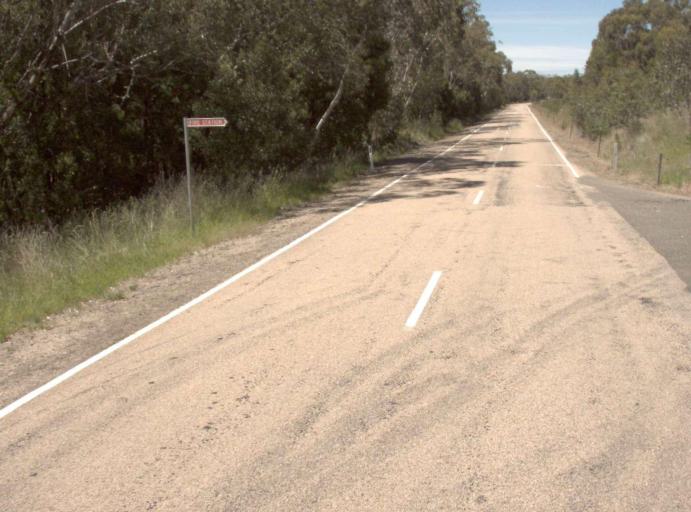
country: AU
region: Victoria
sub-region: East Gippsland
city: Lakes Entrance
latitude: -37.1938
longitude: 148.2693
